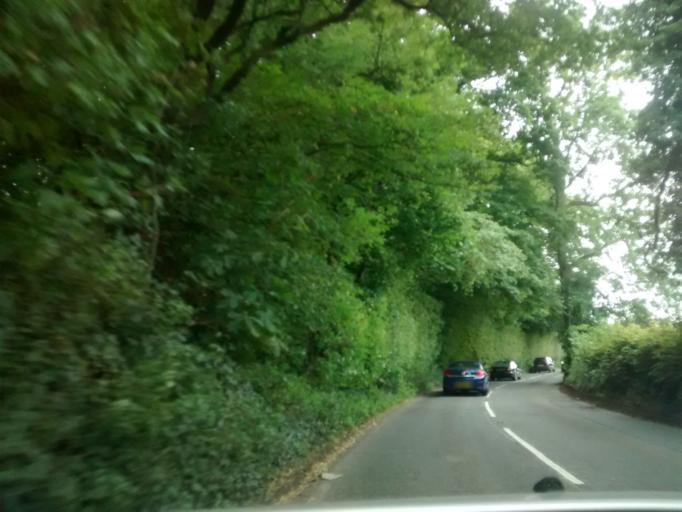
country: GB
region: England
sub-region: South Gloucestershire
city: Cold Ashton
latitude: 51.4337
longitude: -2.3983
